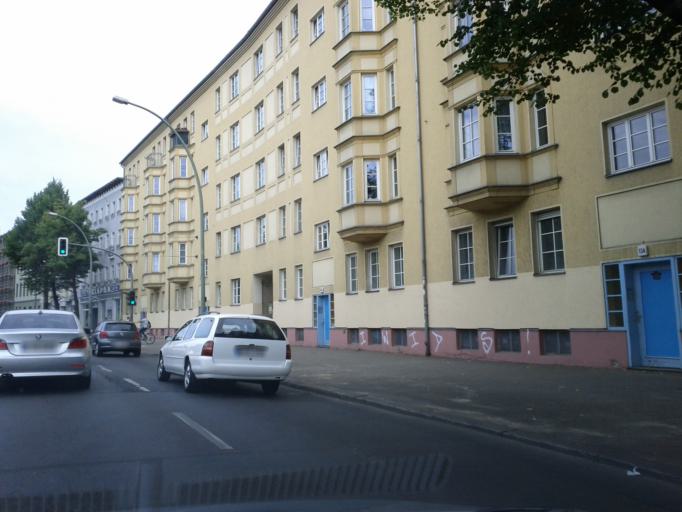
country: DE
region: Berlin
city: Weissensee
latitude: 52.5511
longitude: 13.4636
